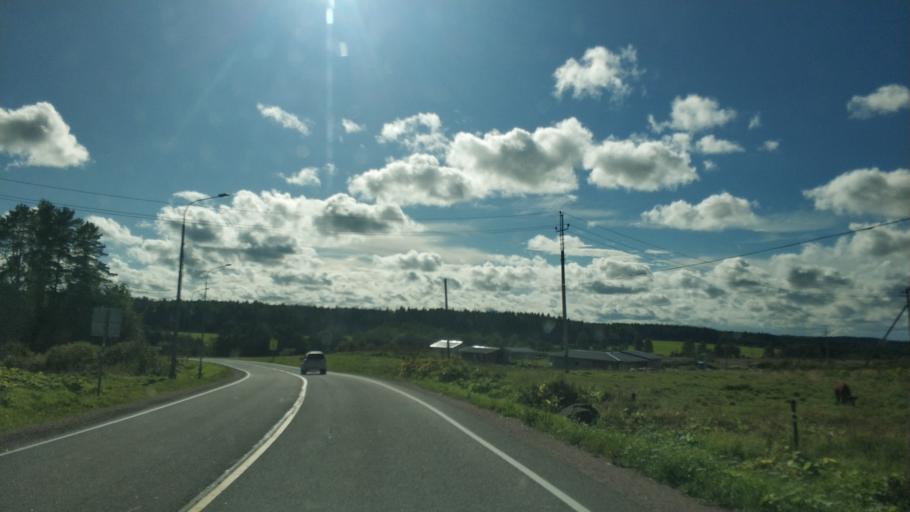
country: RU
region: Republic of Karelia
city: Khelyulya
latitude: 61.6475
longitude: 30.5862
